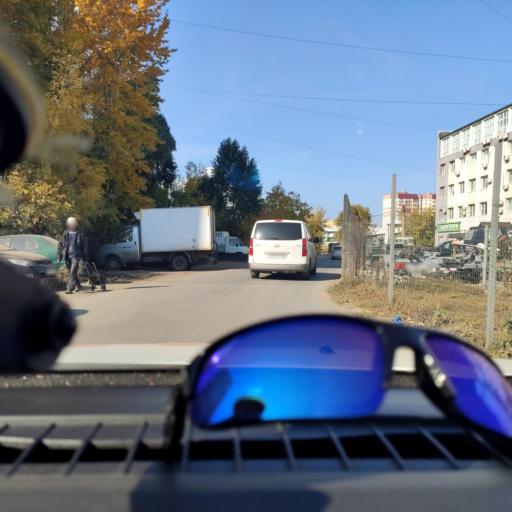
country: RU
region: Samara
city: Samara
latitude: 53.2489
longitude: 50.2139
